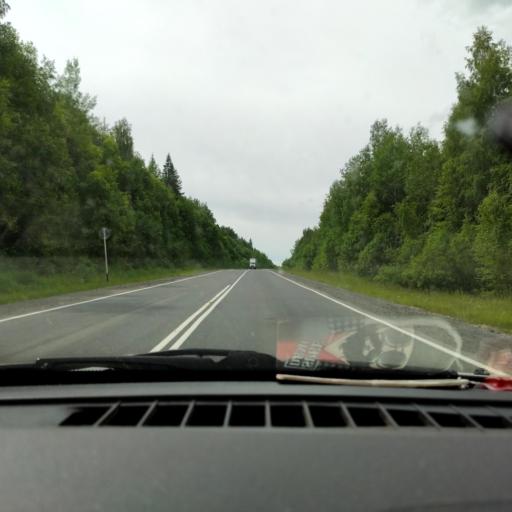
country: RU
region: Perm
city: Chusovoy
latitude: 58.3708
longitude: 58.0301
